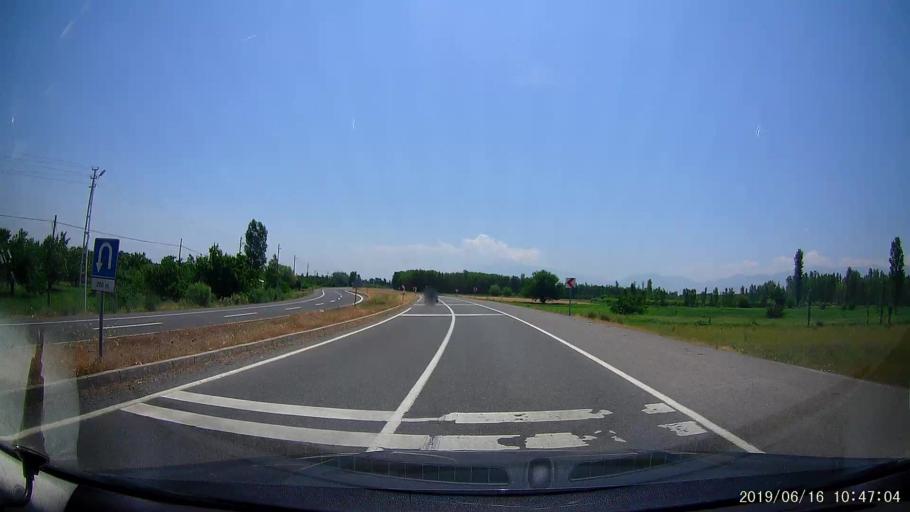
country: AM
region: Armavir
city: Shenavan
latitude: 40.0155
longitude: 43.8839
